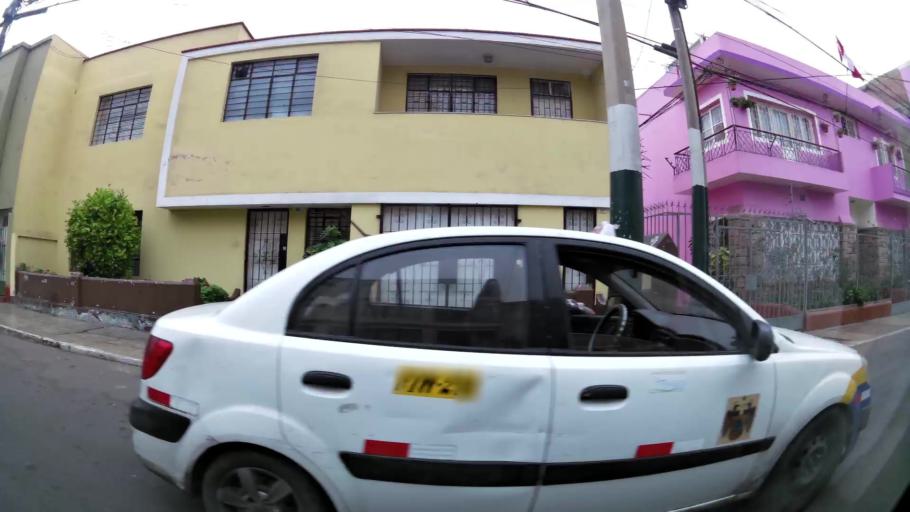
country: PE
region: Callao
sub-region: Callao
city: Callao
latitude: -12.0610
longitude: -77.1276
